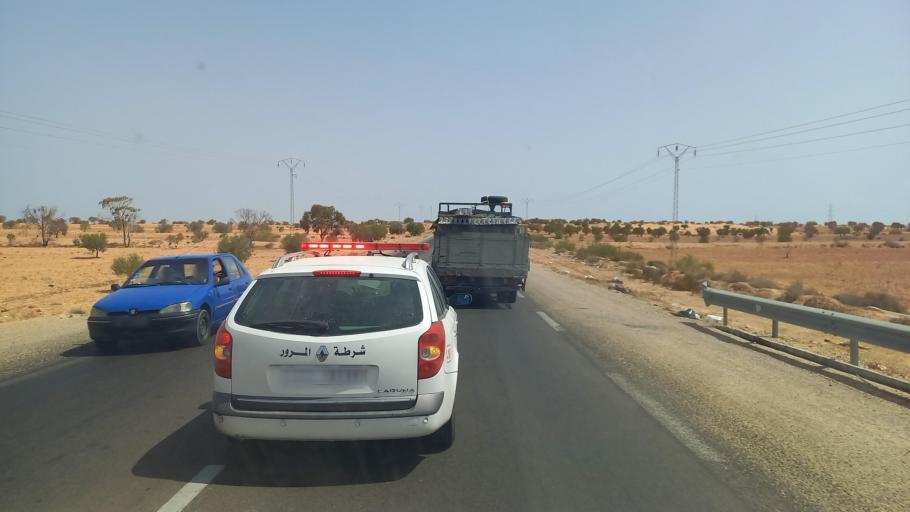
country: TN
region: Madanin
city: Zarzis
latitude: 33.4131
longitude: 10.8682
